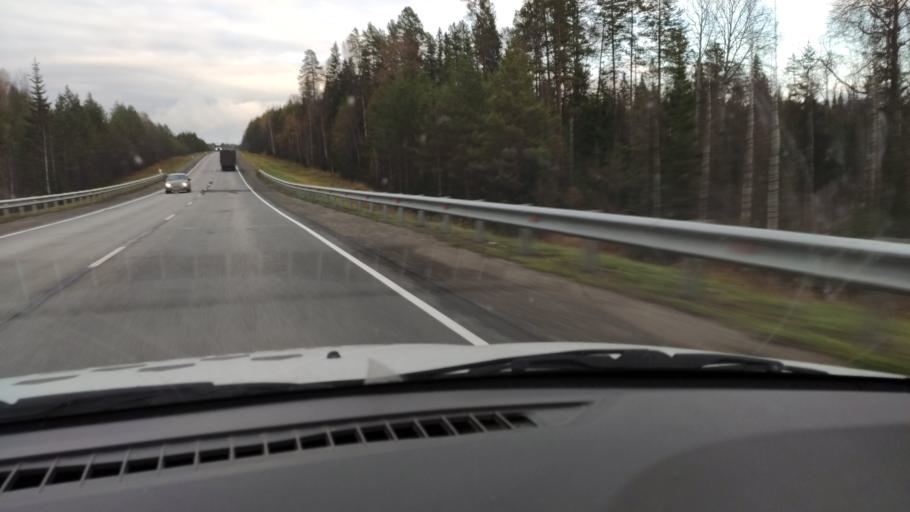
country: RU
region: Kirov
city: Chernaya Kholunitsa
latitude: 58.8258
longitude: 51.7843
